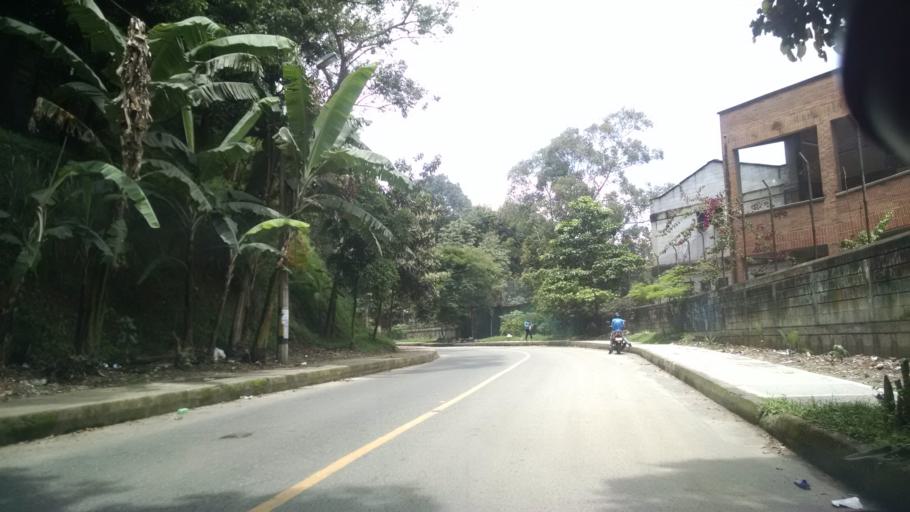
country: CO
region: Antioquia
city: Itagui
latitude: 6.2026
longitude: -75.5904
